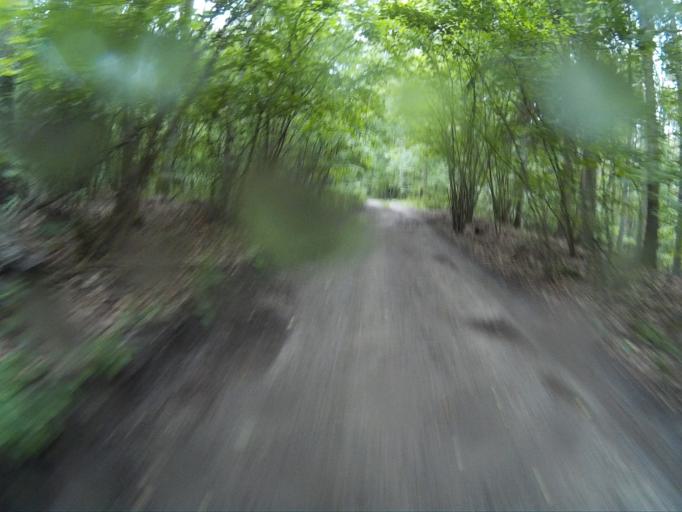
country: PL
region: Kujawsko-Pomorskie
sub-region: Powiat tucholski
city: Gostycyn
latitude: 53.5191
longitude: 17.8736
